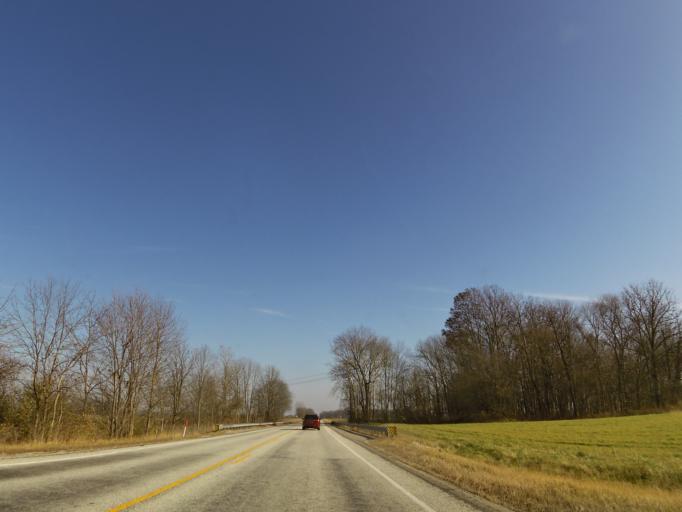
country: US
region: Indiana
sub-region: Shelby County
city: Morristown
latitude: 39.5582
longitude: -85.6609
